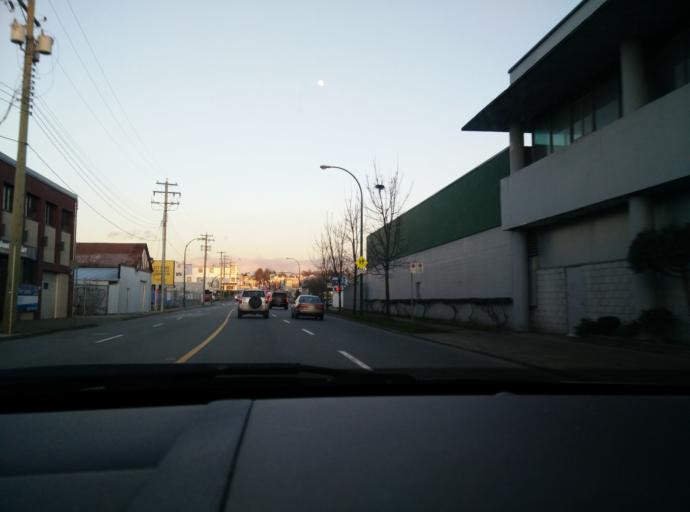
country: CA
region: British Columbia
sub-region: Fraser Valley Regional District
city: North Vancouver
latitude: 49.2768
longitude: -123.0811
